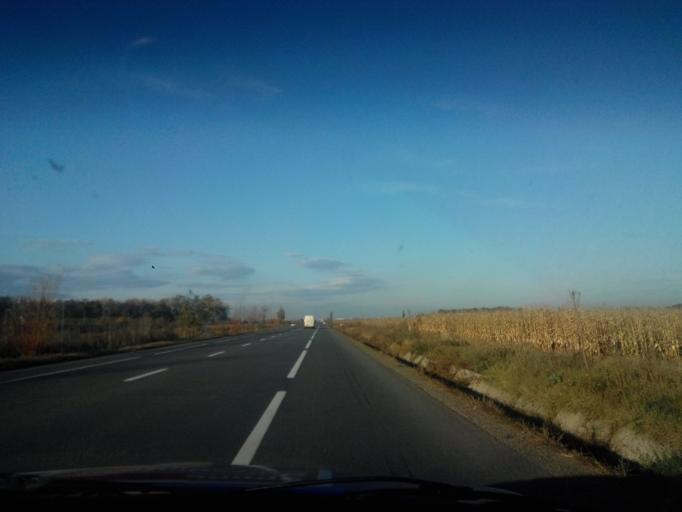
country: RO
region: Neamt
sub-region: Municipiul Roman
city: Roman
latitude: 46.8679
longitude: 26.8937
